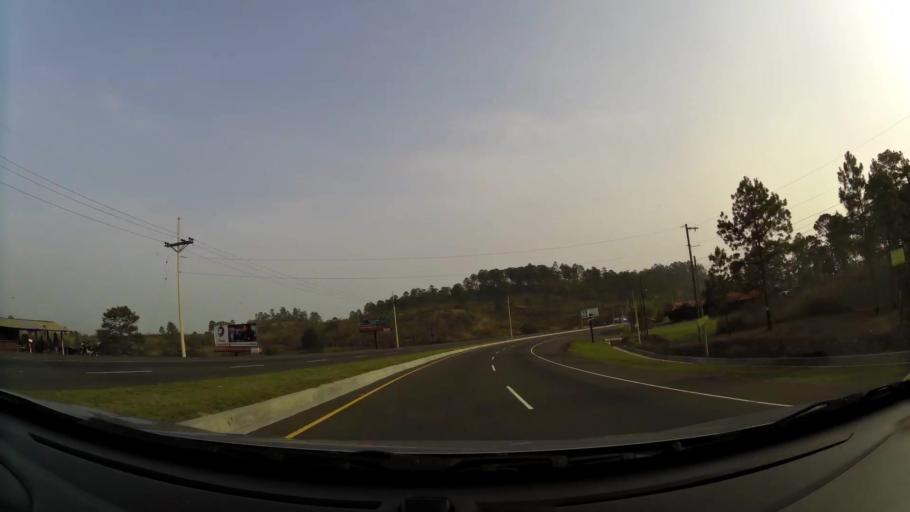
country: HN
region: Francisco Morazan
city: Tamara
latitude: 14.1688
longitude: -87.3136
